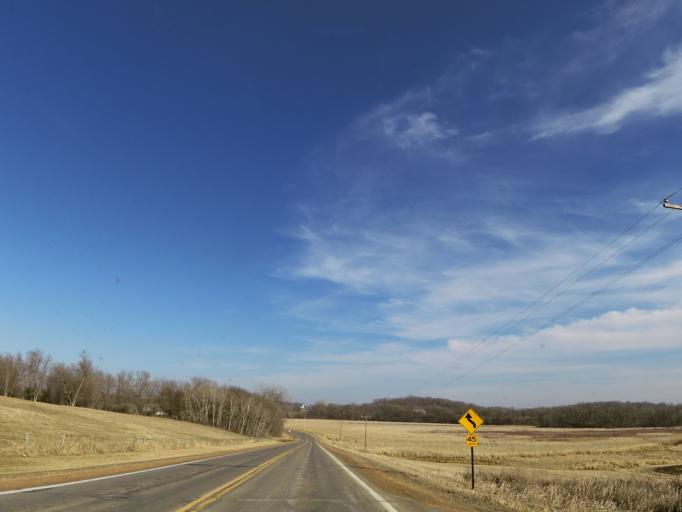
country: US
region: Minnesota
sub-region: Scott County
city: Prior Lake
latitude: 44.6305
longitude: -93.4532
